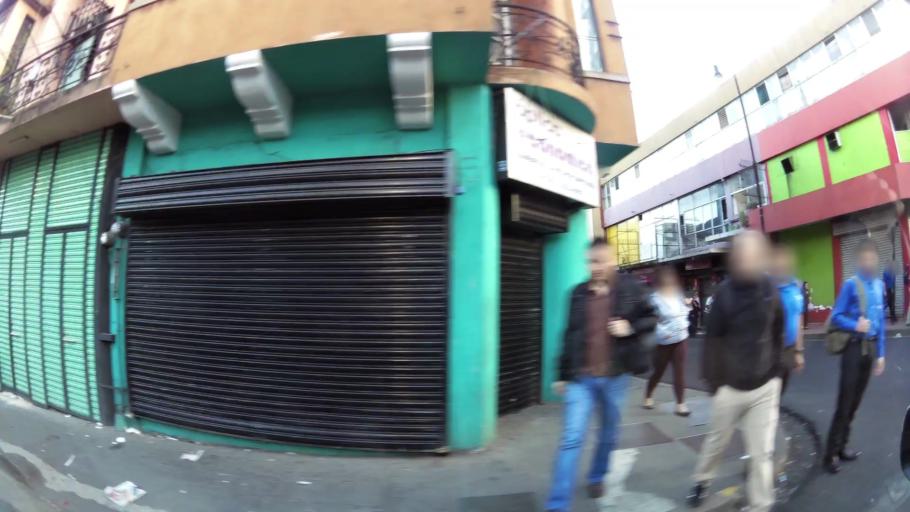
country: CR
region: San Jose
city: San Jose
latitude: 9.9368
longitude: -84.0798
